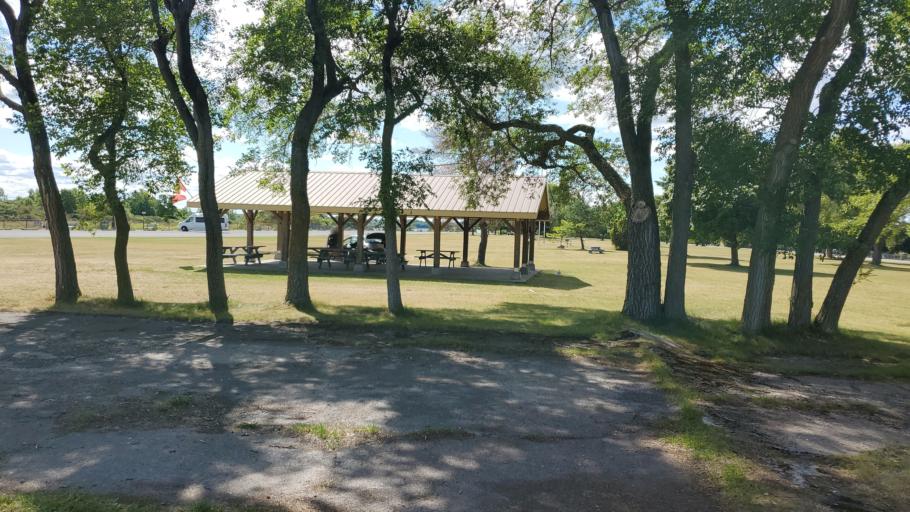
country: US
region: New York
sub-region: St. Lawrence County
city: Ogdensburg
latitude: 44.8322
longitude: -75.3136
